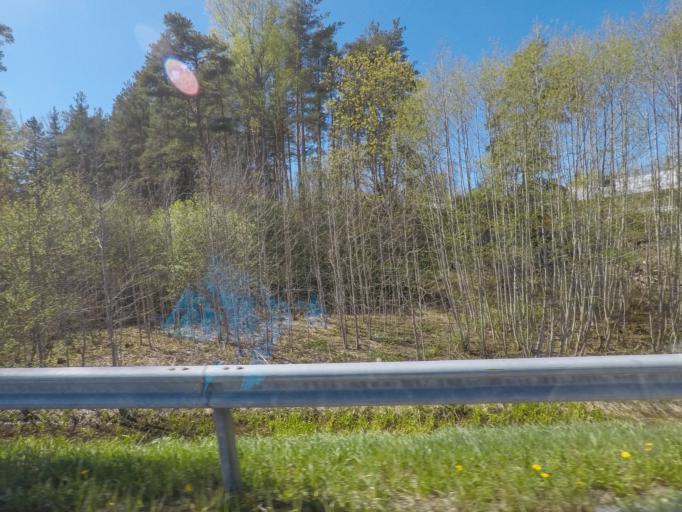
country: FI
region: Uusimaa
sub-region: Helsinki
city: Sammatti
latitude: 60.3581
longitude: 23.8022
